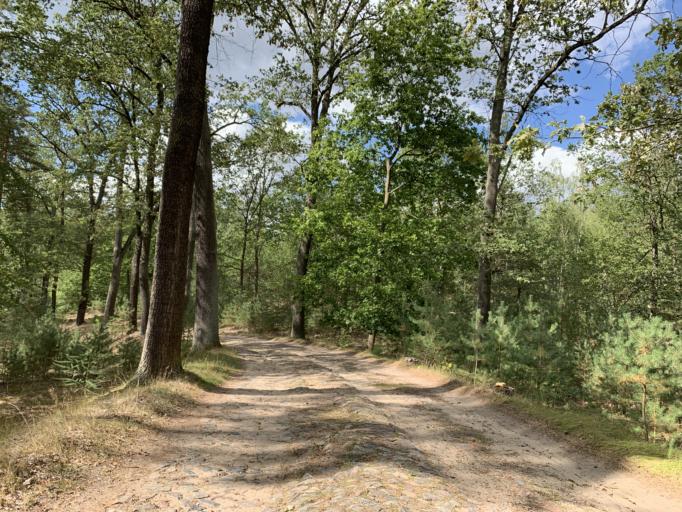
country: DE
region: Brandenburg
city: Michendorf
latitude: 52.3208
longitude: 12.9971
